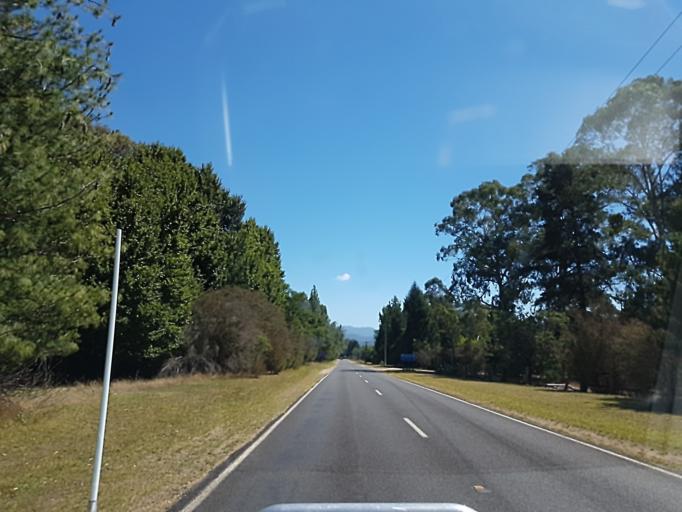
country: AU
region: Victoria
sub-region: Alpine
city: Mount Beauty
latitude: -36.7763
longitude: 147.0320
